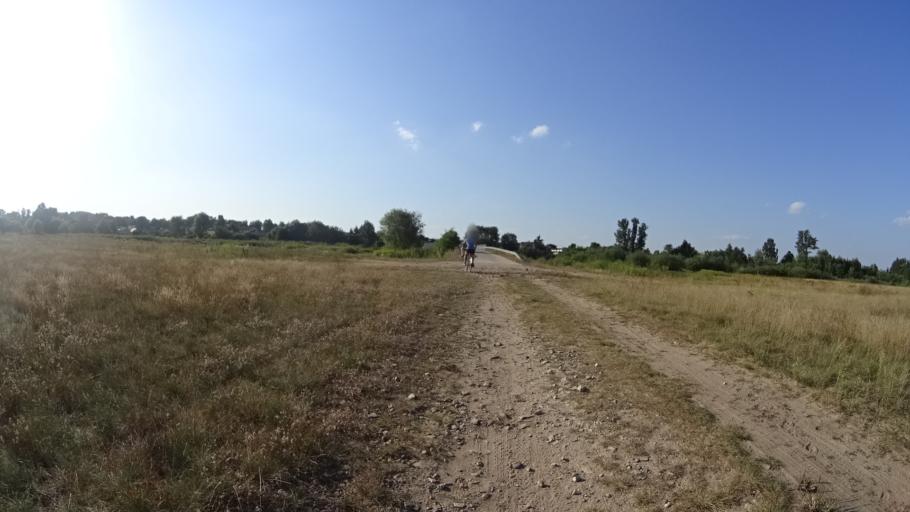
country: PL
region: Masovian Voivodeship
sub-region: Powiat bialobrzeski
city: Wysmierzyce
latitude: 51.6540
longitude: 20.8280
